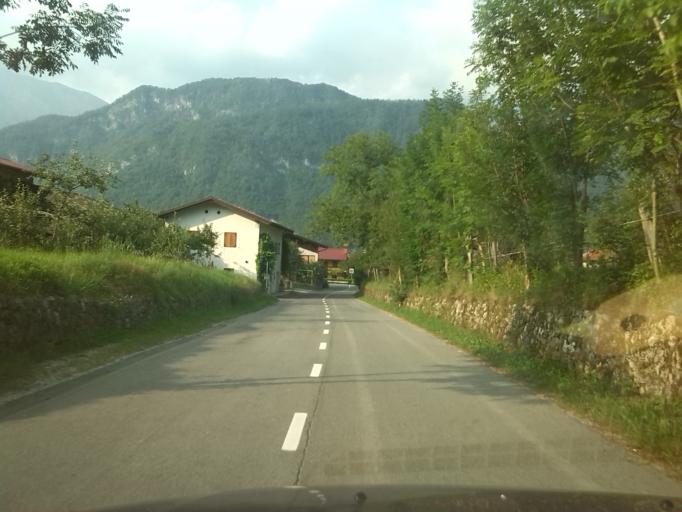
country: SI
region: Kobarid
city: Kobarid
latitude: 46.2311
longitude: 13.5920
